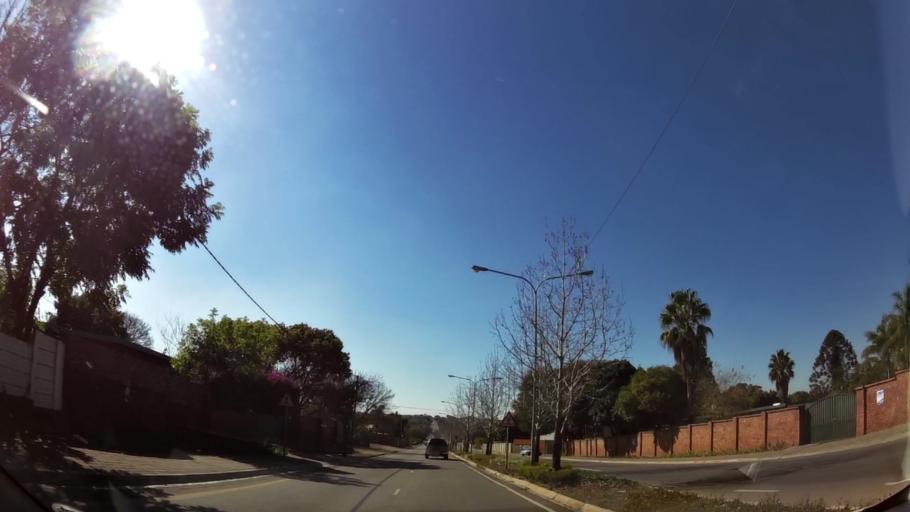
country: ZA
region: Gauteng
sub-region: City of Tshwane Metropolitan Municipality
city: Centurion
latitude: -25.8432
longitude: 28.2051
